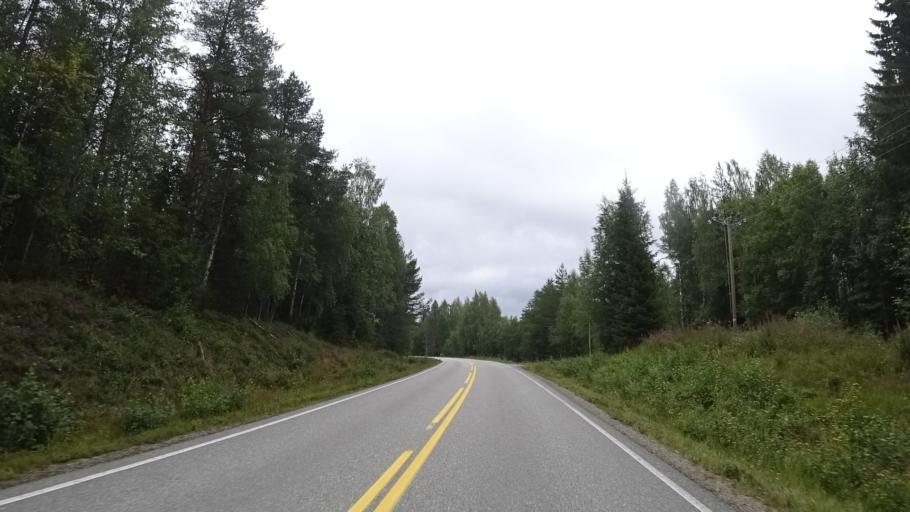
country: FI
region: North Karelia
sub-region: Joensuu
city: Ilomantsi
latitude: 63.2595
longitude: 30.6664
